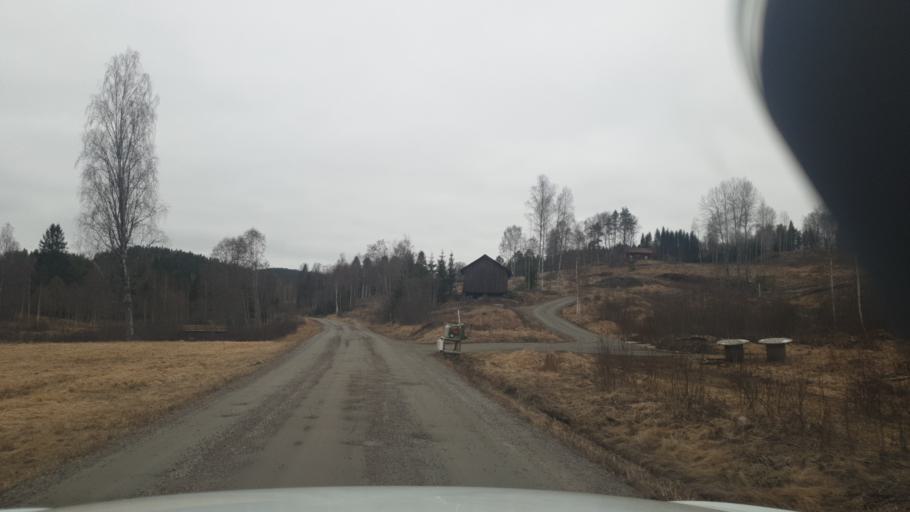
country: NO
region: Ostfold
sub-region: Romskog
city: Romskog
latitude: 59.6773
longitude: 11.9336
